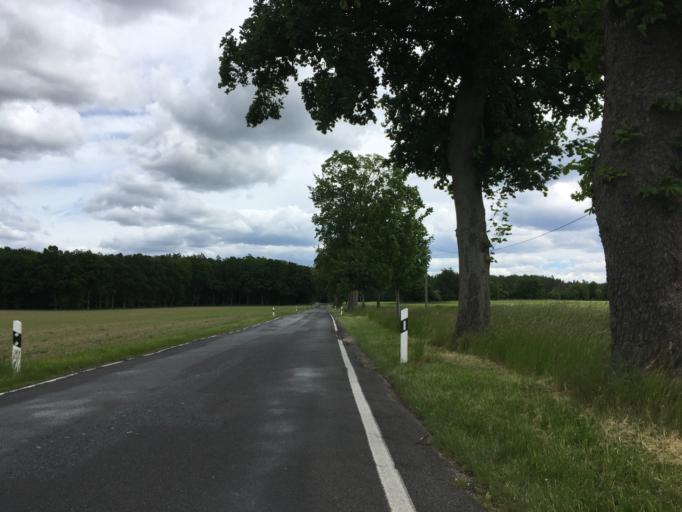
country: DE
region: Brandenburg
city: Werftpfuhl
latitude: 52.7303
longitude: 13.8010
